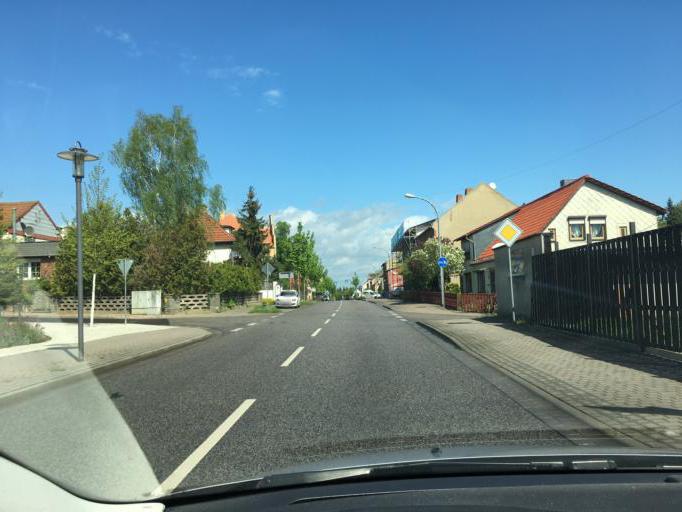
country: DE
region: Saxony-Anhalt
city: Haldensleben I
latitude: 52.2671
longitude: 11.4216
